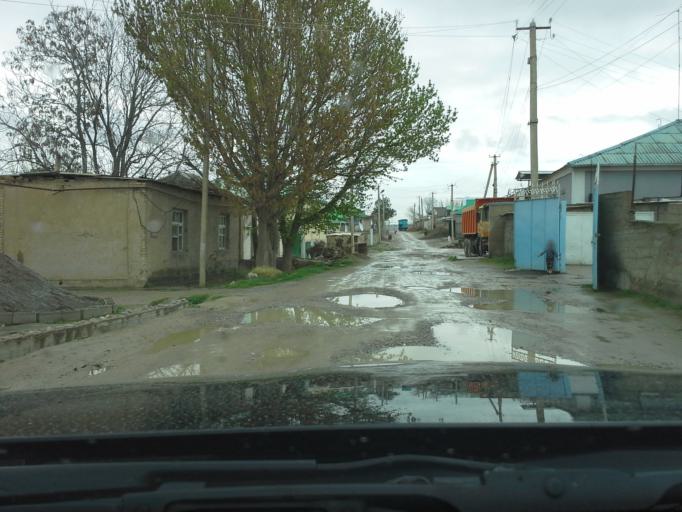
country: TM
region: Ahal
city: Abadan
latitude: 37.9622
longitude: 58.2090
